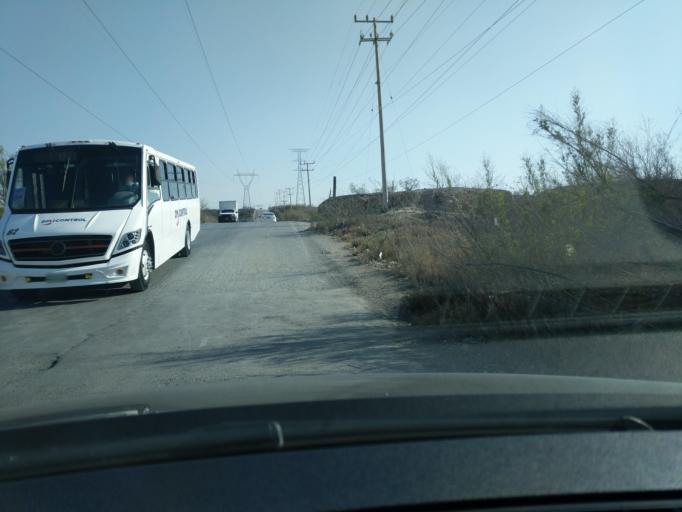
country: MX
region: Coahuila
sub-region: Ramos Arizpe
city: Ramos Arizpe
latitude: 25.5389
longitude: -100.9780
